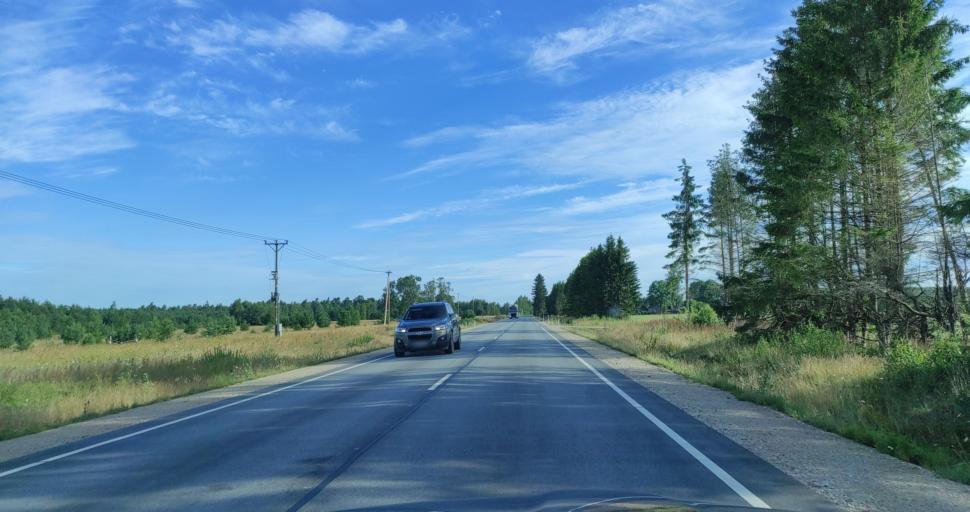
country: LV
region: Pavilostas
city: Pavilosta
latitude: 56.8102
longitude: 21.2258
